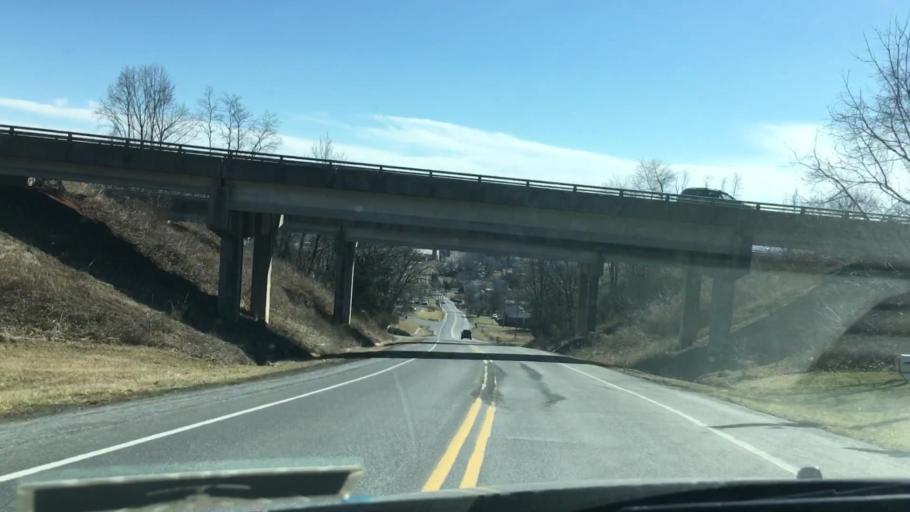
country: US
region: Pennsylvania
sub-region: Lancaster County
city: Reamstown
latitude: 40.1827
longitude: -76.1315
